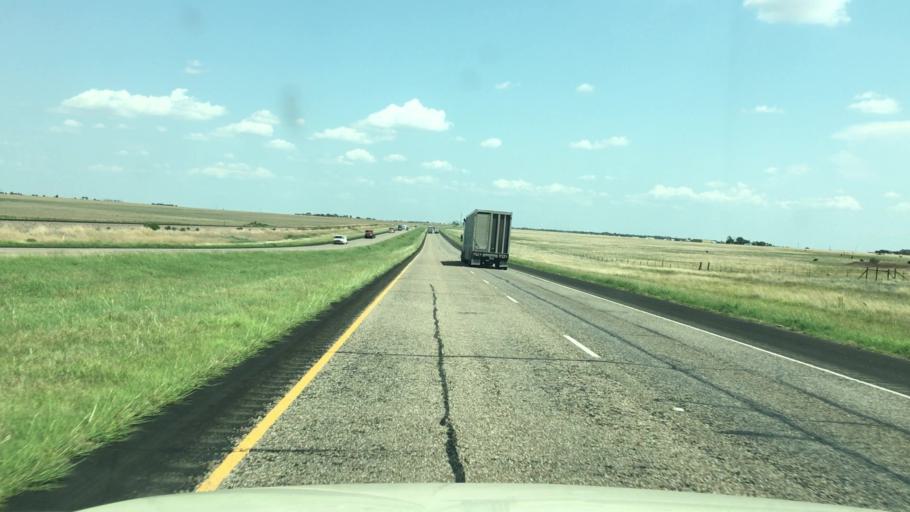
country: US
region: Texas
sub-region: Armstrong County
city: Claude
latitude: 35.1296
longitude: -101.4108
